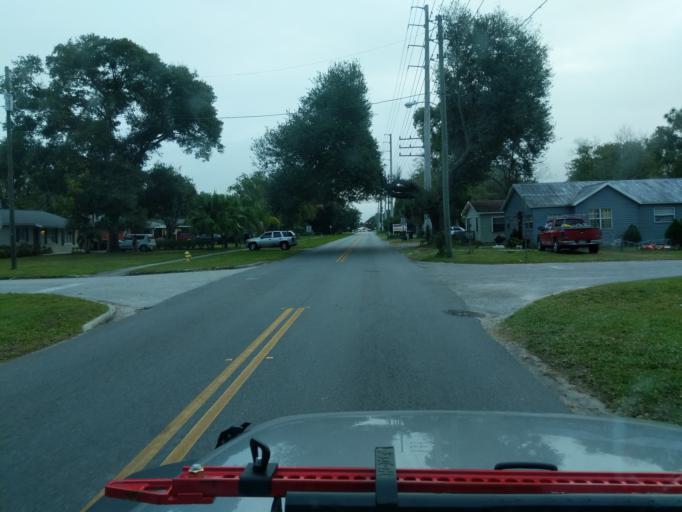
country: US
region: Florida
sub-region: Orange County
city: Winter Garden
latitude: 28.5584
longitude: -81.5796
